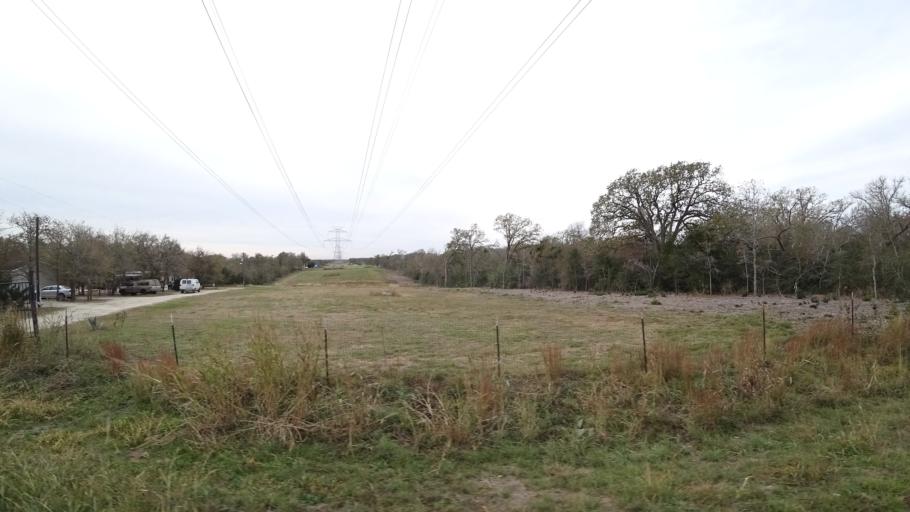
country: US
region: Texas
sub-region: Travis County
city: Garfield
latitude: 30.1047
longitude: -97.5674
